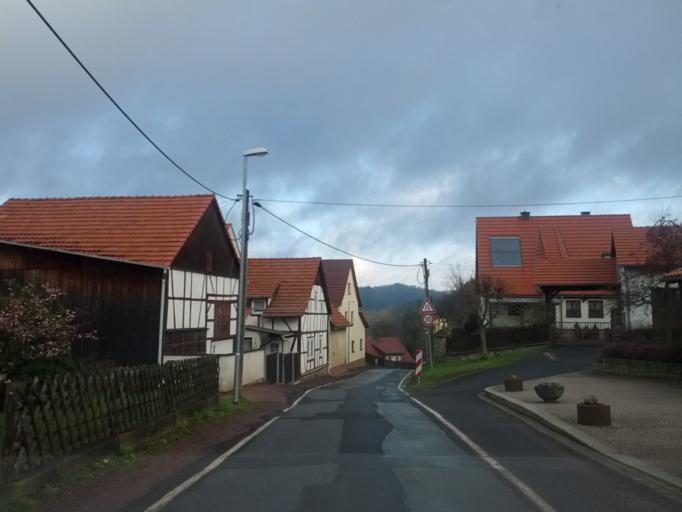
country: DE
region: Thuringia
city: Wolfsburg-Unkeroda
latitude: 50.9303
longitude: 10.2641
